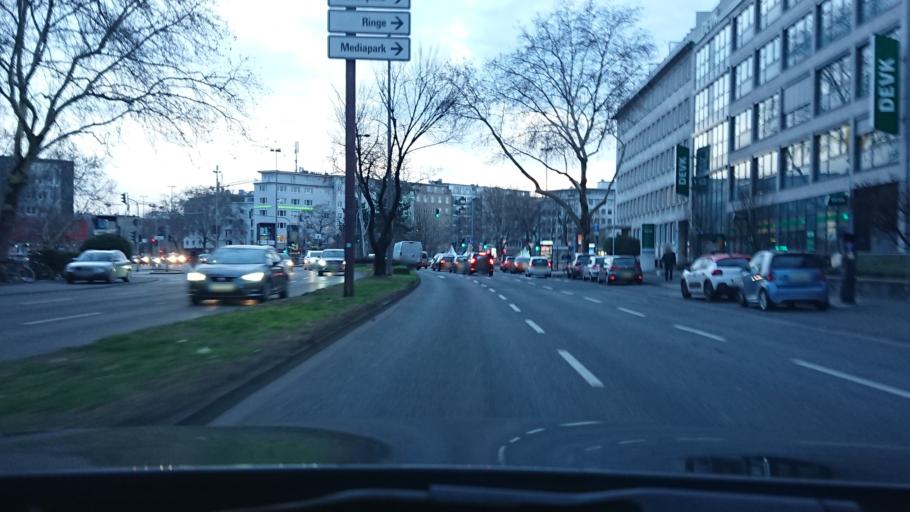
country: DE
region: North Rhine-Westphalia
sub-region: Regierungsbezirk Koln
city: Neustadt/Nord
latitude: 50.9516
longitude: 6.9598
